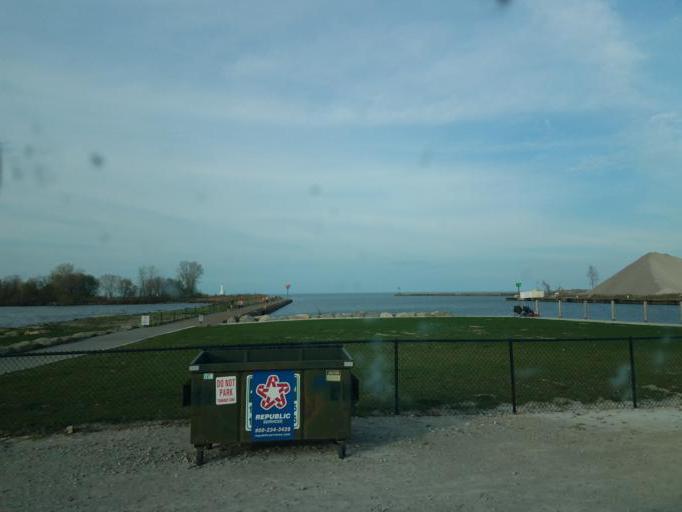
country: US
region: Ohio
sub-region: Erie County
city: Huron
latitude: 41.3978
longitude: -82.5508
